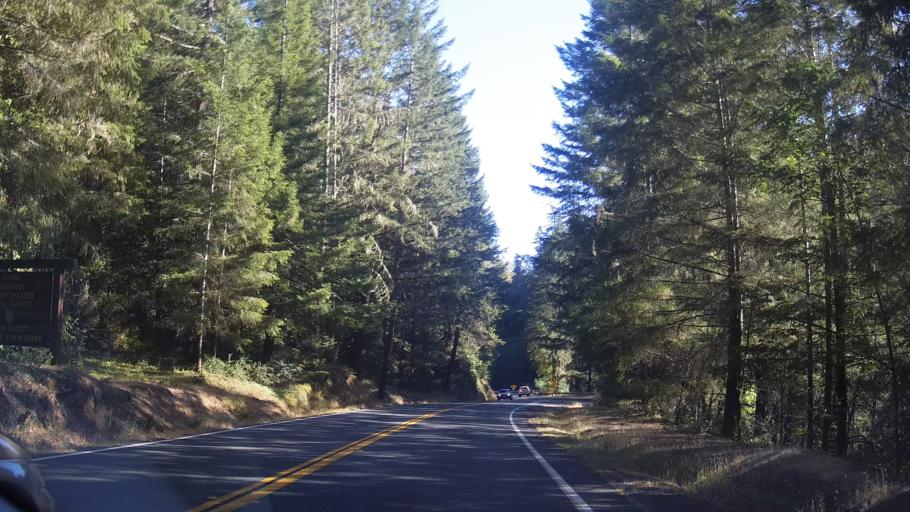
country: US
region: California
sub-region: Mendocino County
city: Brooktrails
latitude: 39.3559
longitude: -123.5096
